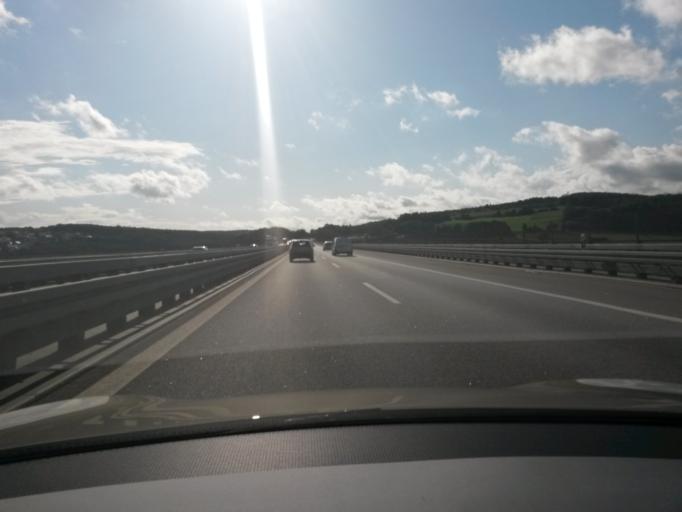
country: DE
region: Bavaria
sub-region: Upper Palatinate
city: Sinzing
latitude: 48.9979
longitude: 12.0367
